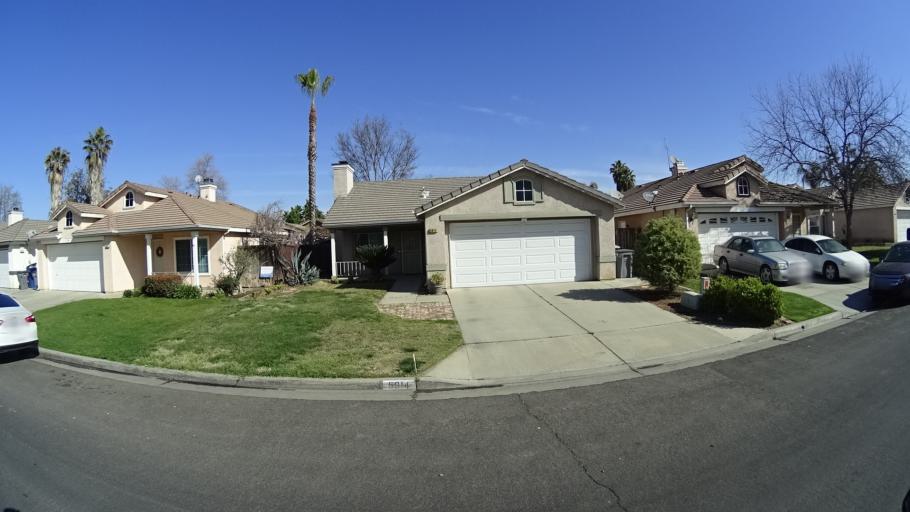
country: US
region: California
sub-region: Fresno County
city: West Park
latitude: 36.7981
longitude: -119.8918
